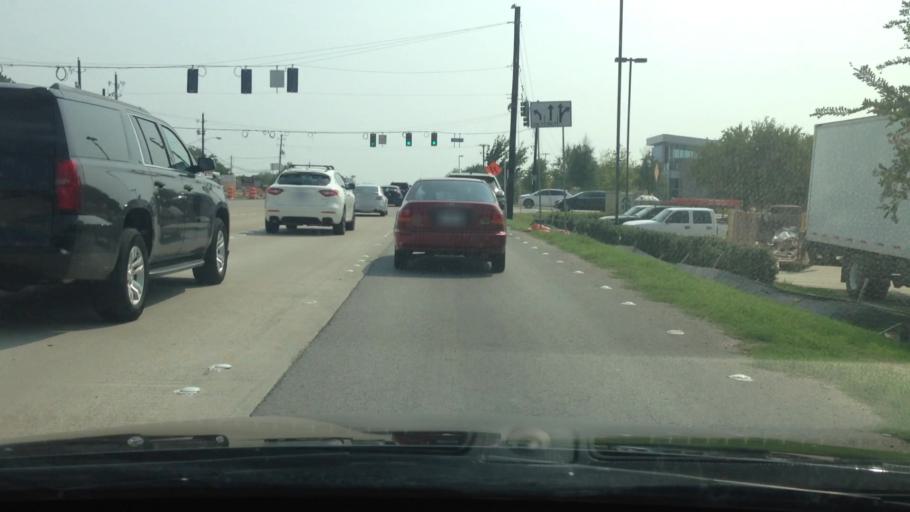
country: US
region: Texas
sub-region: Tarrant County
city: Colleyville
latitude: 32.8897
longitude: -97.1499
